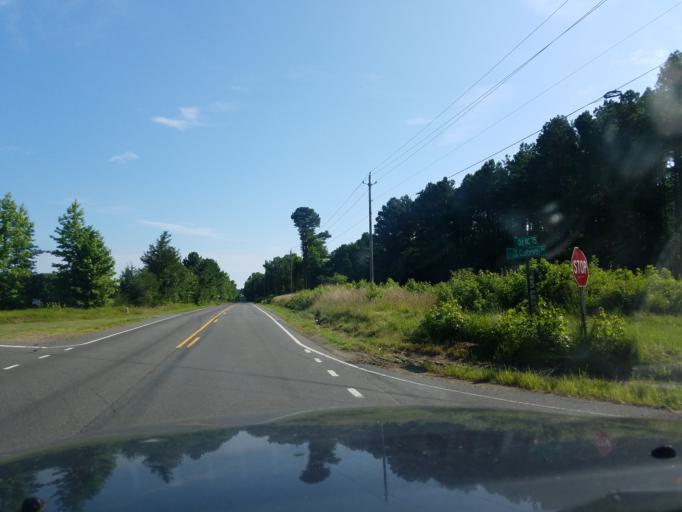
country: US
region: North Carolina
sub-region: Granville County
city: Butner
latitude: 36.2150
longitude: -78.7245
